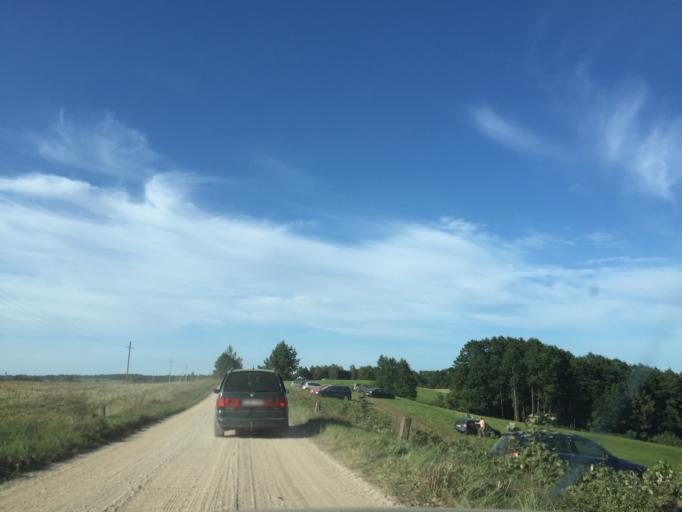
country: LT
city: Zarasai
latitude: 55.7894
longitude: 25.9539
